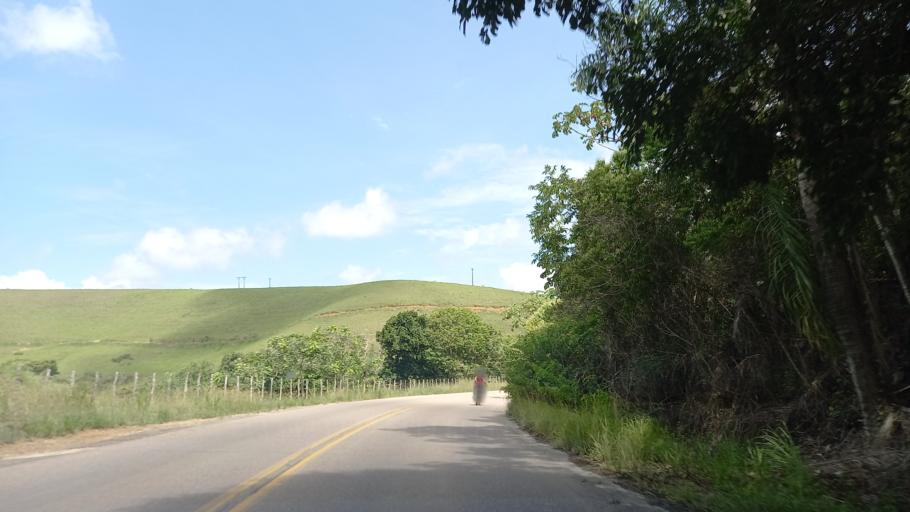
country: BR
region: Pernambuco
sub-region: Rio Formoso
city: Rio Formoso
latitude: -8.7384
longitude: -35.1720
